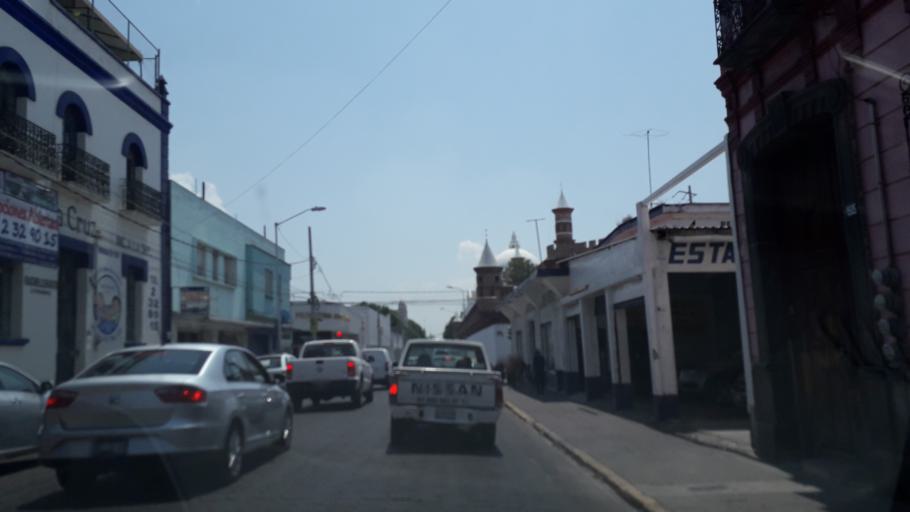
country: MX
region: Puebla
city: Puebla
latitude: 19.0498
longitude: -98.2093
